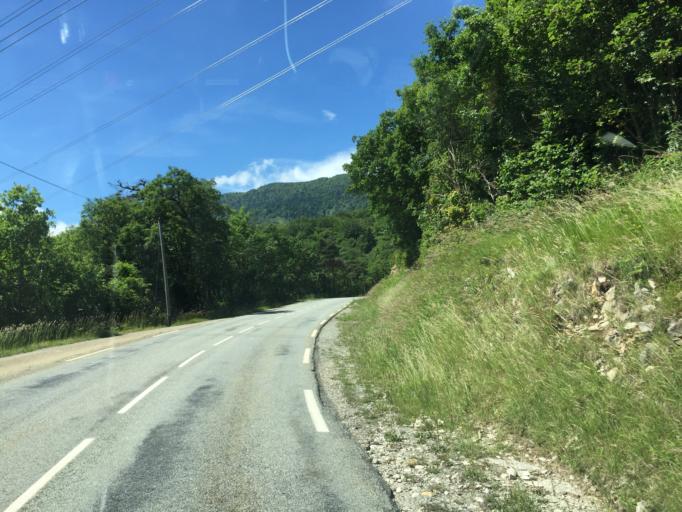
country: FR
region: Rhone-Alpes
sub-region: Departement de la Savoie
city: Saint-Baldoph
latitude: 45.5100
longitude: 5.9256
